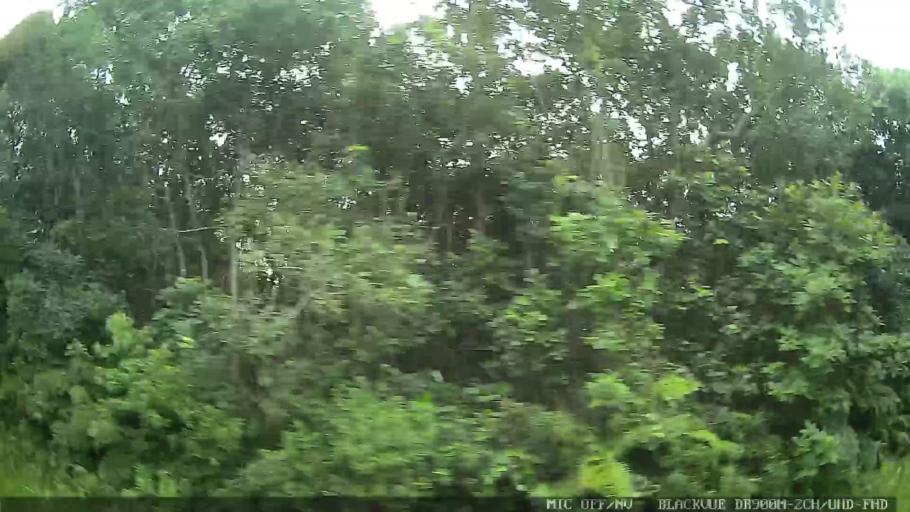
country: BR
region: Sao Paulo
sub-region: Iguape
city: Iguape
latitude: -24.6853
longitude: -47.4721
